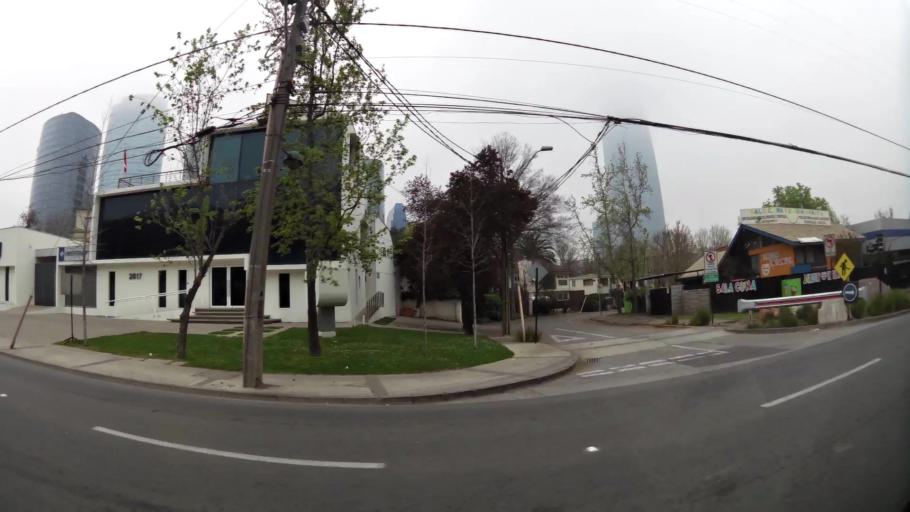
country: CL
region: Santiago Metropolitan
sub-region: Provincia de Santiago
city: Villa Presidente Frei, Nunoa, Santiago, Chile
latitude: -33.4129
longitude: -70.6084
